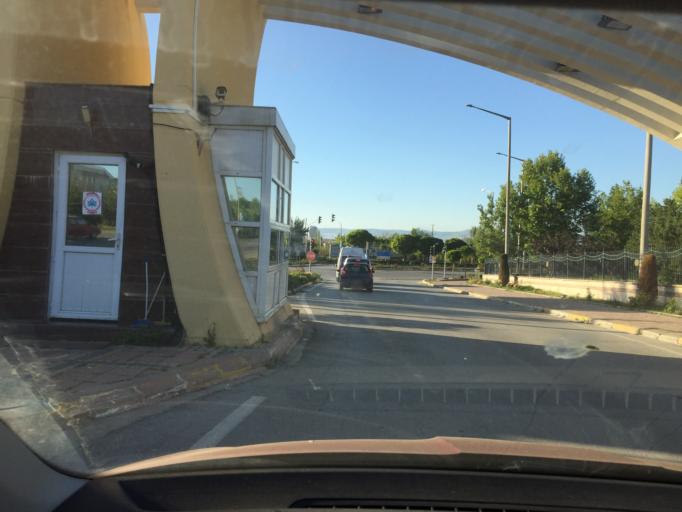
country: TR
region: Eskisehir
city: Eskisehir
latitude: 39.7541
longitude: 30.4882
